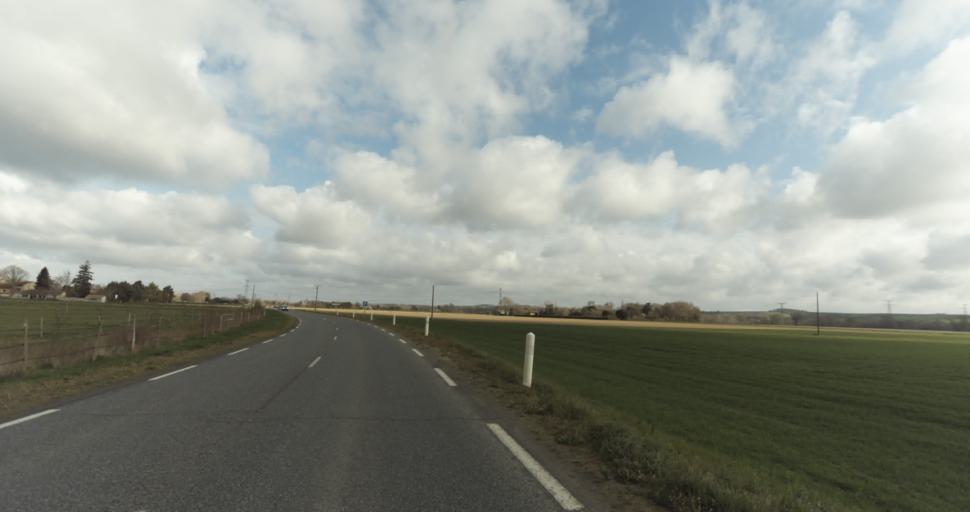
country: FR
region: Midi-Pyrenees
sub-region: Departement de la Haute-Garonne
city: Miremont
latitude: 43.3776
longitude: 1.4458
